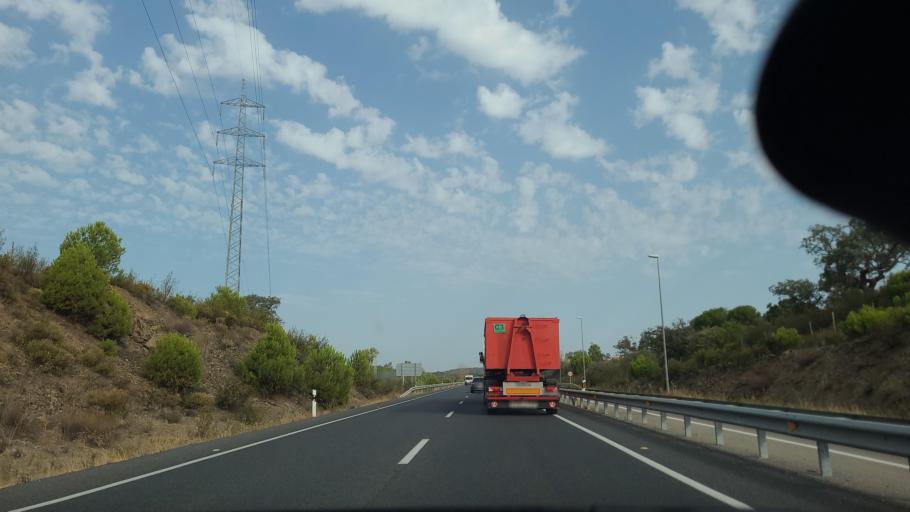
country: ES
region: Andalusia
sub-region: Province of Cordoba
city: Villaharta
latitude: 38.0896
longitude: -4.8631
